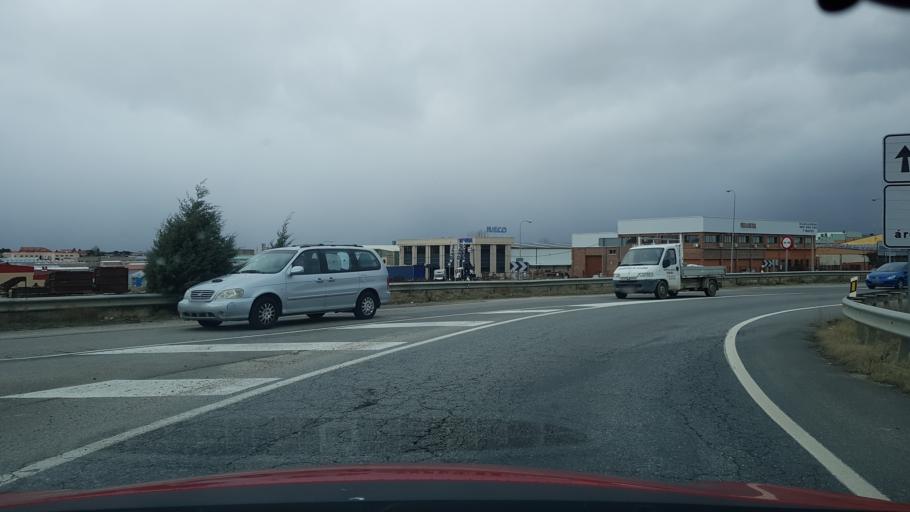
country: ES
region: Castille and Leon
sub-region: Provincia de Segovia
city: Segovia
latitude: 40.9050
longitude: -4.1045
